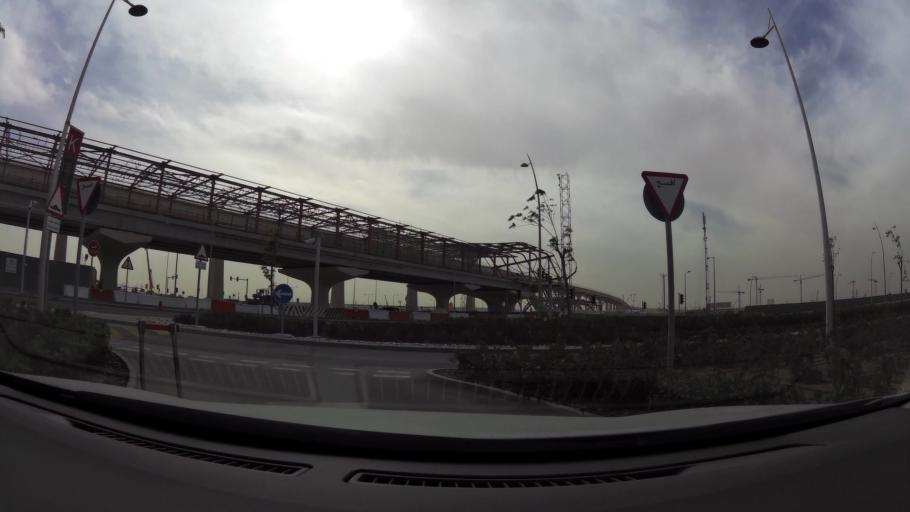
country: QA
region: Baladiyat ar Rayyan
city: Ar Rayyan
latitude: 25.3254
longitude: 51.3473
